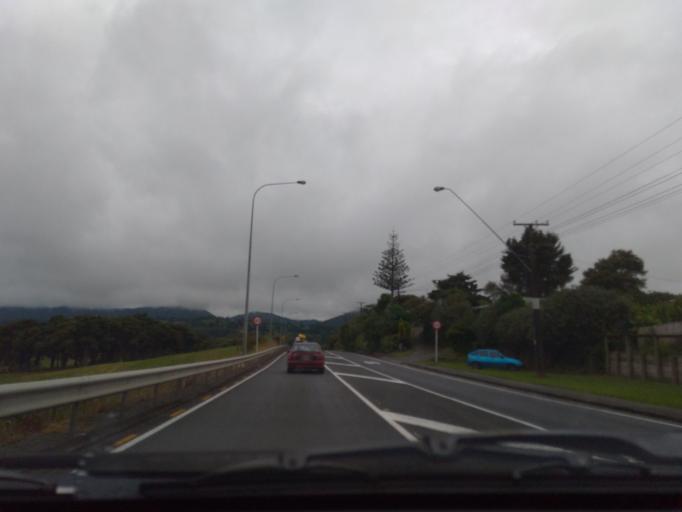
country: NZ
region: Auckland
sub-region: Auckland
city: Wellsford
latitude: -36.1693
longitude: 174.4465
